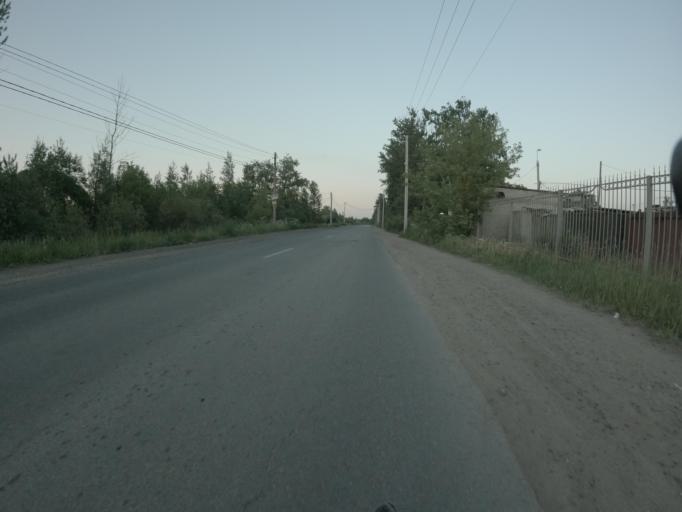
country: RU
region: St.-Petersburg
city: Dachnoye
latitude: 59.8226
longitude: 30.2856
